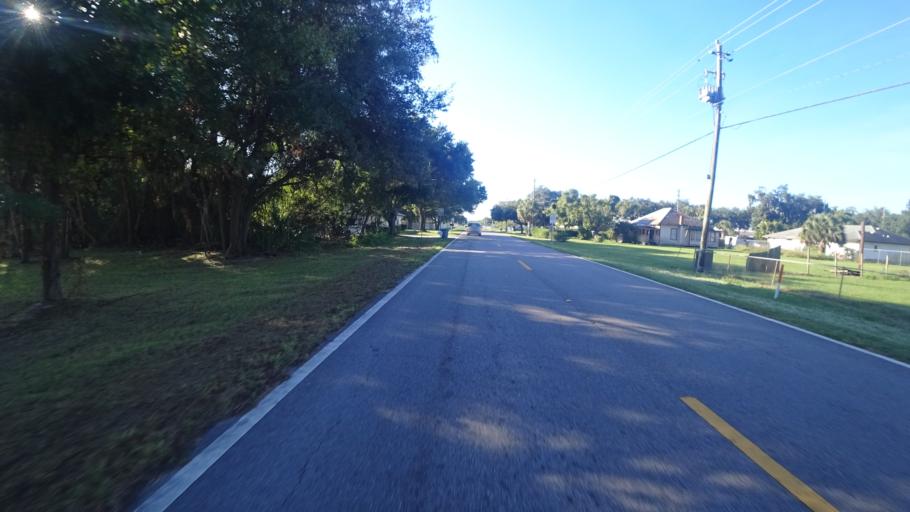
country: US
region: Florida
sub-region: Manatee County
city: Memphis
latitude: 27.5688
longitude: -82.5565
